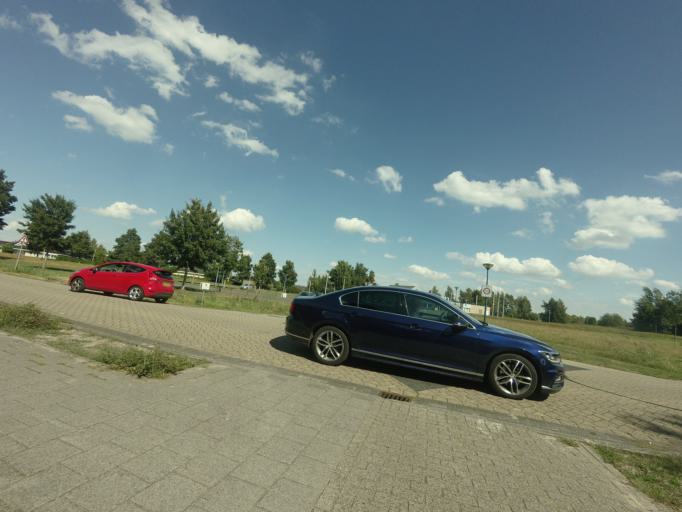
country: NL
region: Drenthe
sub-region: Gemeente Hoogeveen
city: Hoogeveen
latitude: 52.5923
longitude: 6.4606
